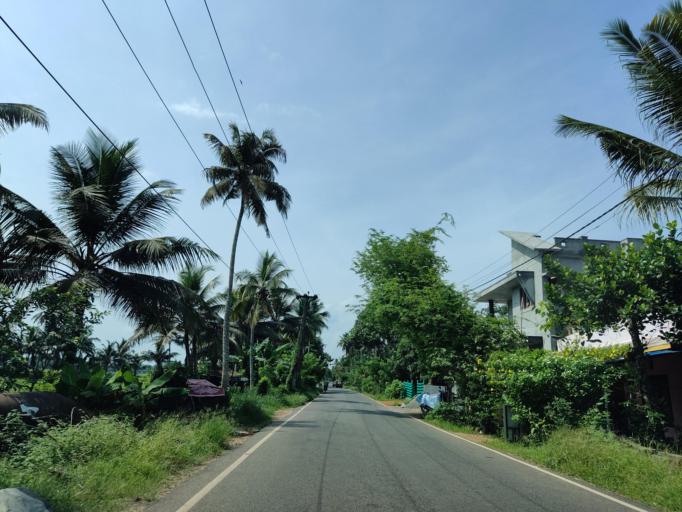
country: IN
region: Kerala
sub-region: Pattanamtitta
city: Tiruvalla
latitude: 9.3430
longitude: 76.4682
